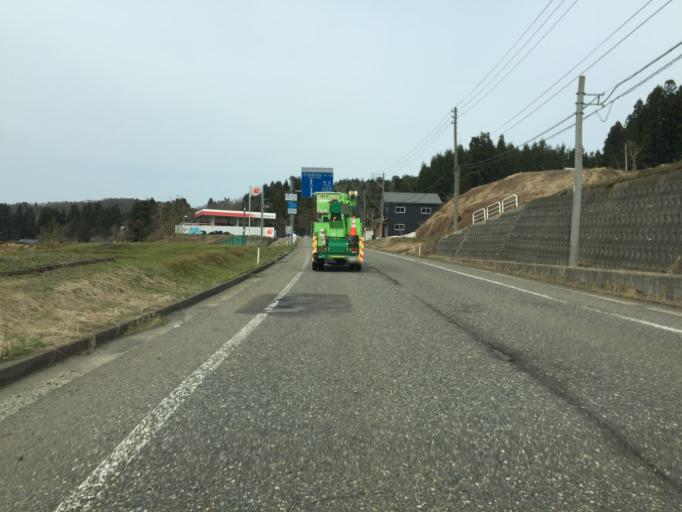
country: JP
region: Niigata
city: Tochio-honcho
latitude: 37.4567
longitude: 138.9700
